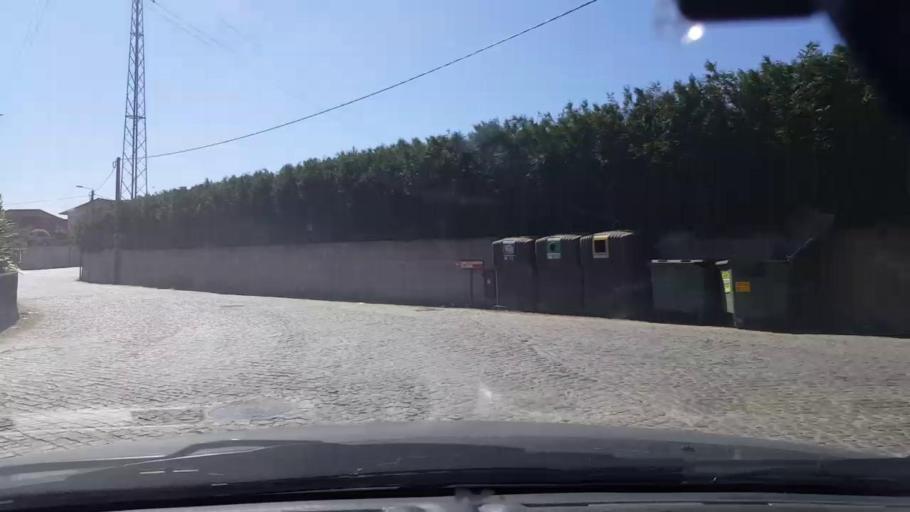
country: PT
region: Porto
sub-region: Matosinhos
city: Lavra
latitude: 41.2809
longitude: -8.7021
